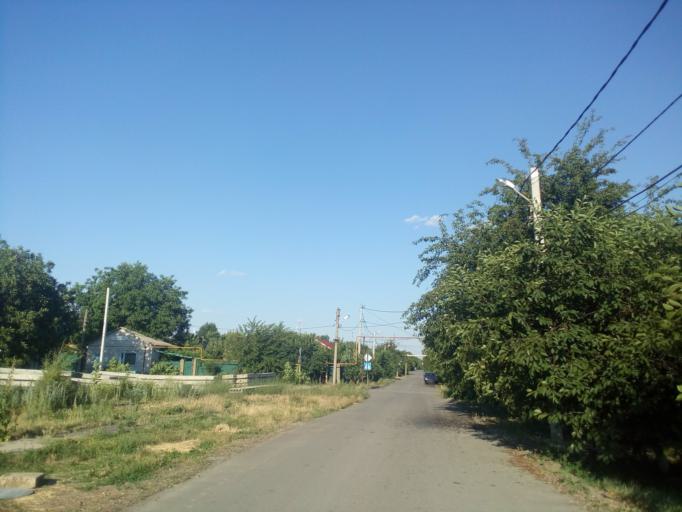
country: RU
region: Rostov
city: Sholokhovskiy
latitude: 48.2781
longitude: 41.0445
